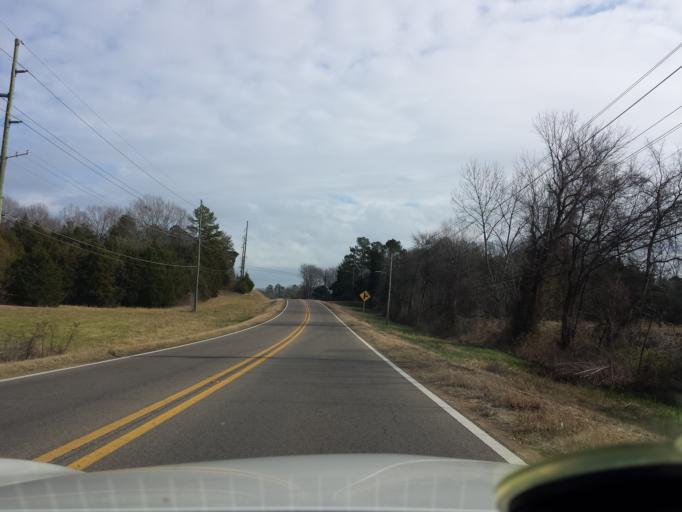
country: US
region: Mississippi
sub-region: Oktibbeha County
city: Starkville
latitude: 33.4621
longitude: -88.8403
